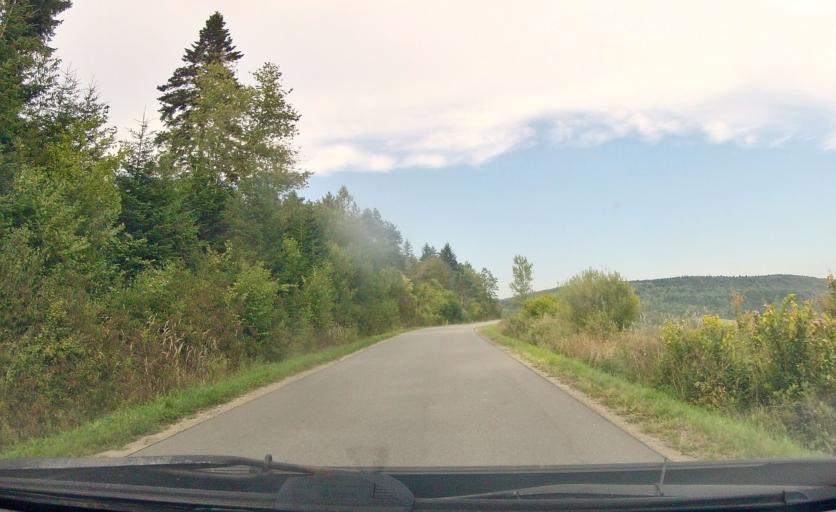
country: PL
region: Subcarpathian Voivodeship
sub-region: Powiat krosnienski
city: Dukla
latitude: 49.5052
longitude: 21.6246
